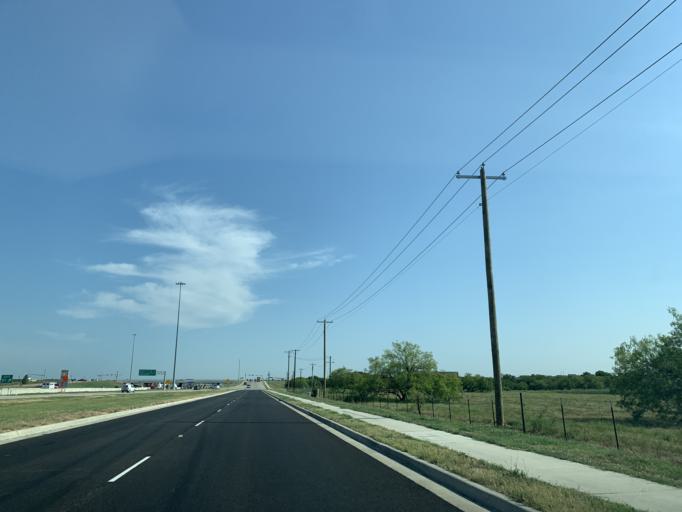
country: US
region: Texas
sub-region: Tarrant County
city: Blue Mound
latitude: 32.8934
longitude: -97.3165
